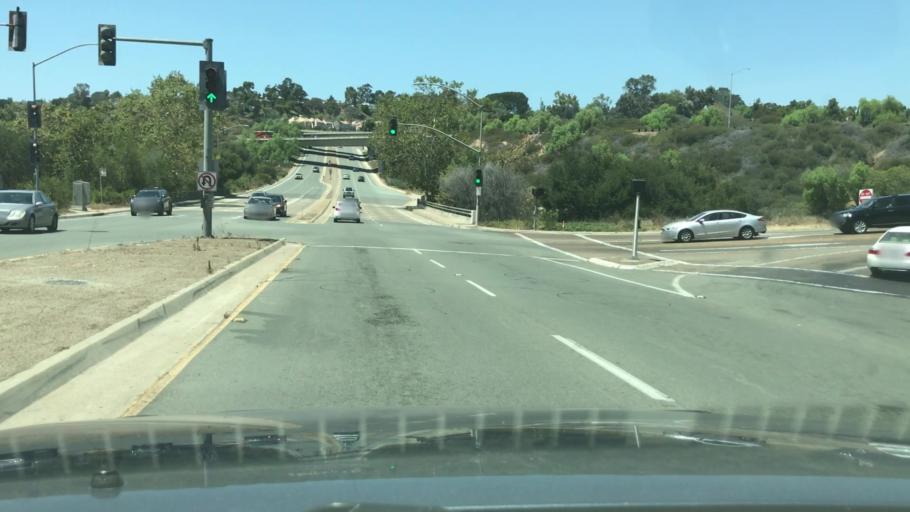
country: US
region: California
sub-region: San Diego County
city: La Jolla
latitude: 32.8445
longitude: -117.1995
